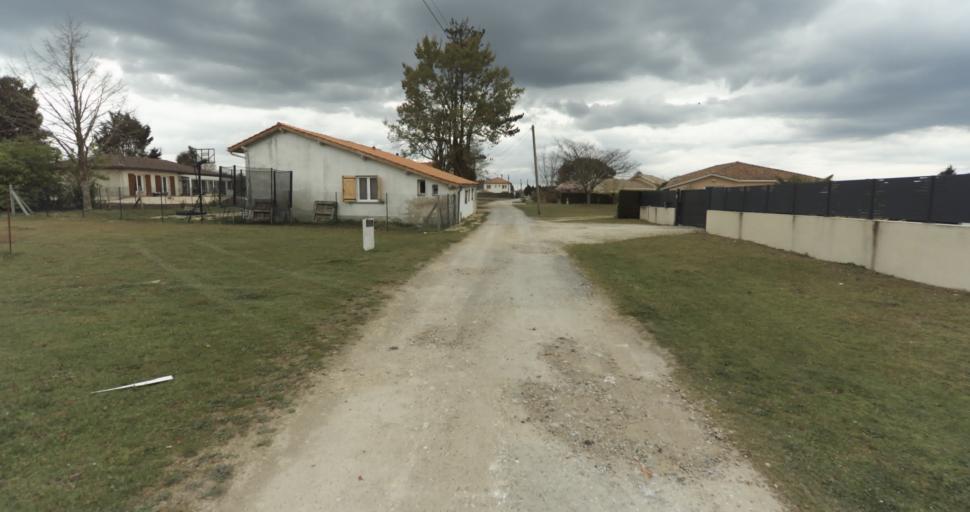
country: FR
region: Aquitaine
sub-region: Departement des Landes
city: Roquefort
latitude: 44.0267
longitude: -0.3312
